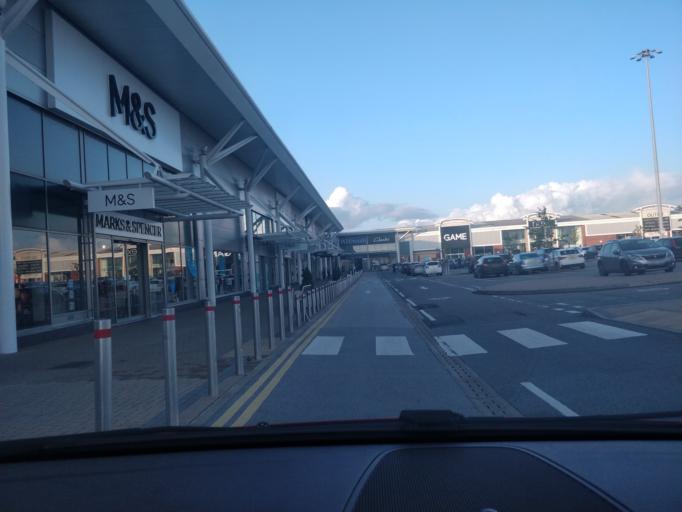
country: GB
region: England
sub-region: Lancashire
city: Preston
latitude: 53.7741
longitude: -2.6790
